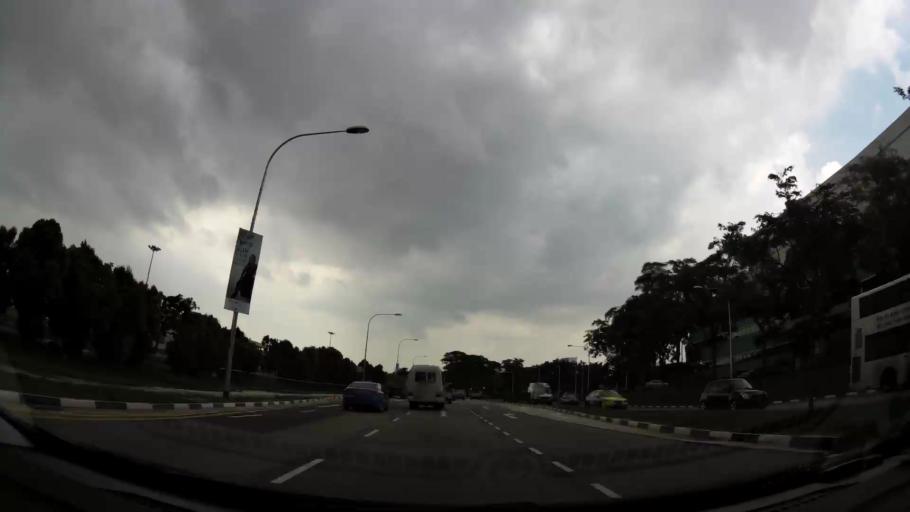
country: SG
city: Singapore
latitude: 1.3304
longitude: 103.9601
